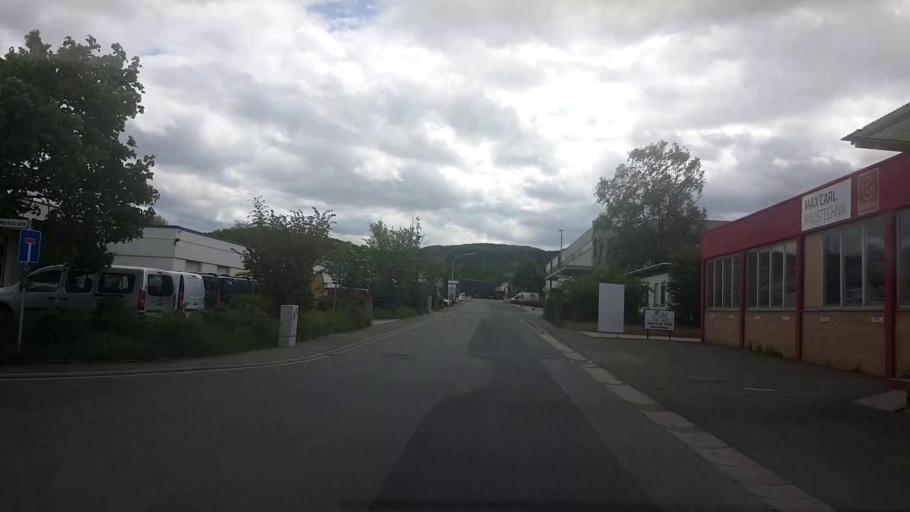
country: DE
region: Bavaria
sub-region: Upper Franconia
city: Lichtenfels
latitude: 50.1341
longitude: 11.0423
